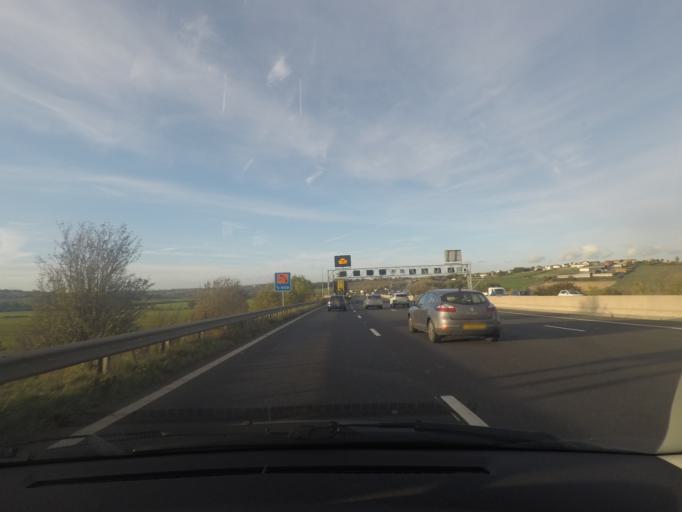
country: GB
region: England
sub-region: City and Borough of Wakefield
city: Ossett
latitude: 53.6927
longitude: -1.5575
